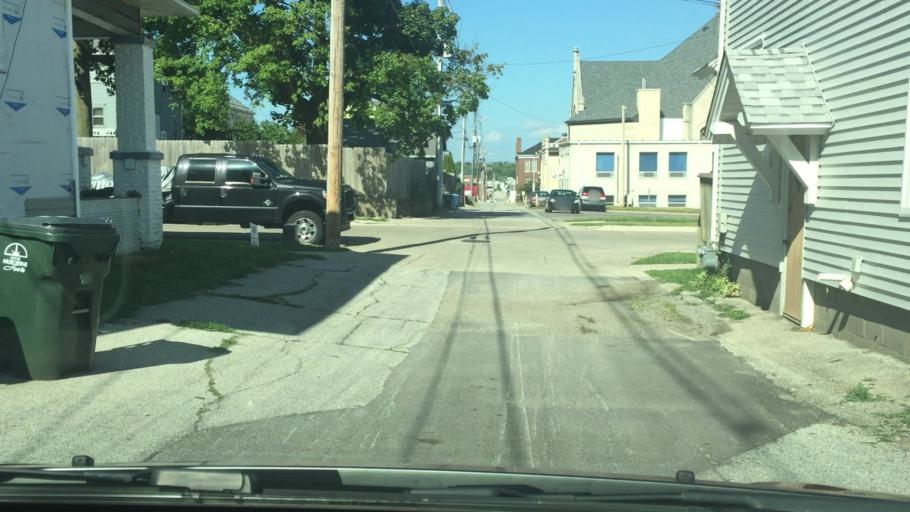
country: US
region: Iowa
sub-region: Muscatine County
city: Muscatine
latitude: 41.4225
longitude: -91.0490
